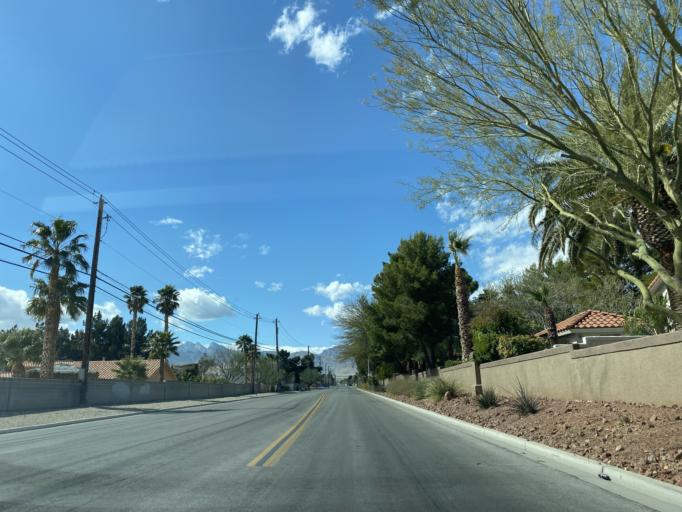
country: US
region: Nevada
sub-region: Clark County
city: Spring Valley
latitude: 36.2556
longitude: -115.2719
